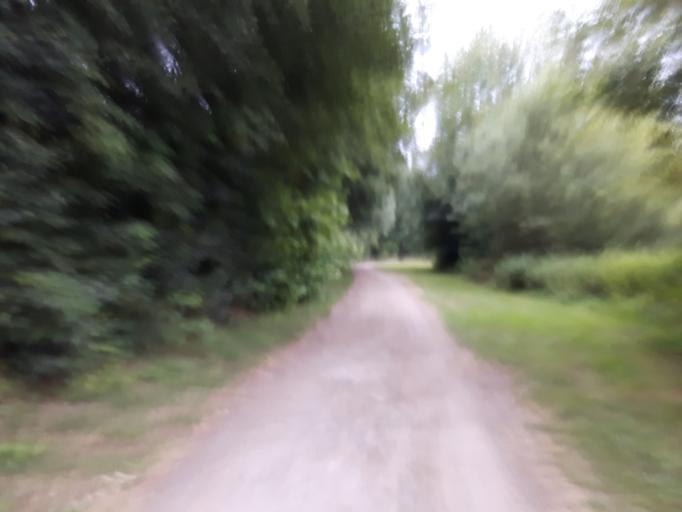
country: DE
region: Lower Saxony
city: Delmenhorst
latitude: 53.0164
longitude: 8.6623
